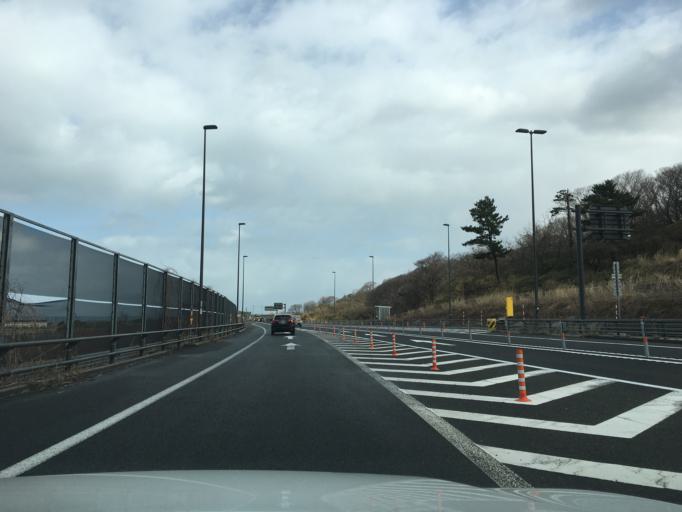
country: JP
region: Yamagata
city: Yuza
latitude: 39.2967
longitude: 139.9766
